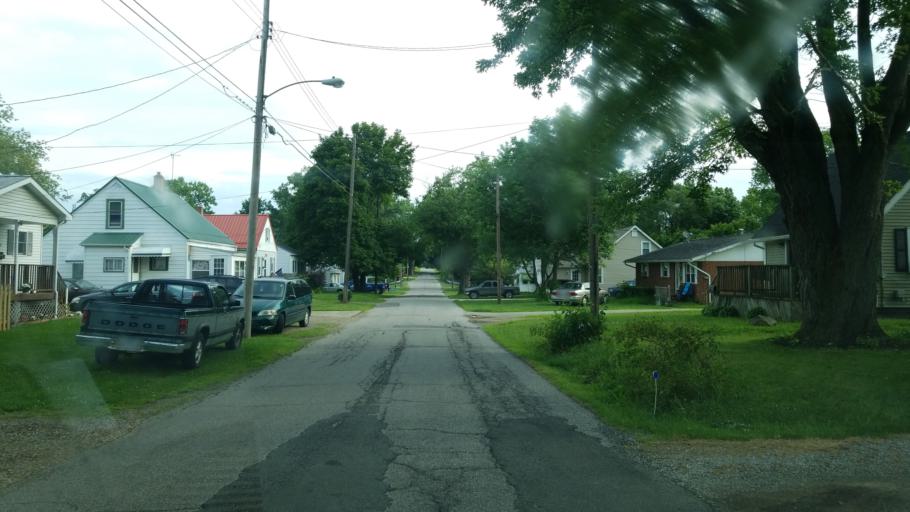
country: US
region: Ohio
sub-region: Ashland County
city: Ashland
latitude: 40.8675
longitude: -82.2998
